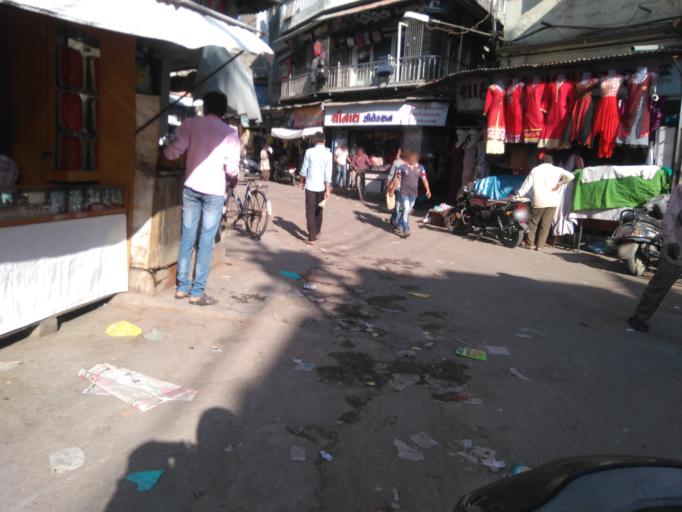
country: IN
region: Gujarat
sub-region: Junagadh
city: Junagadh
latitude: 21.5193
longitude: 70.4625
